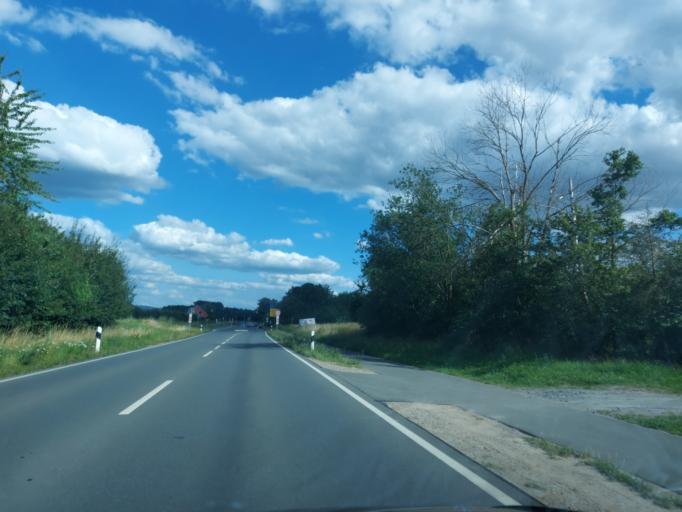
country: DE
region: Lower Saxony
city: Bad Rothenfelde
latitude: 52.1257
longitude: 8.1570
